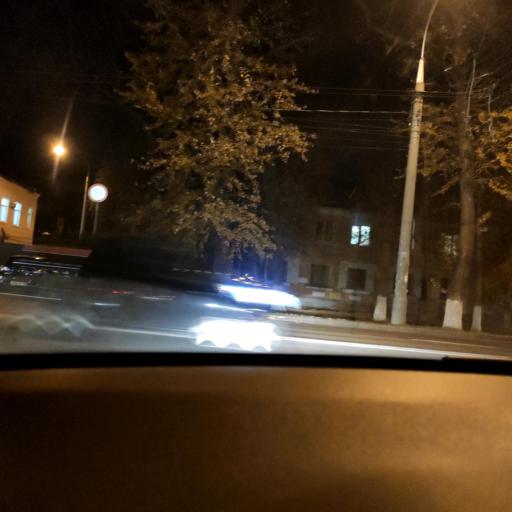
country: RU
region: Samara
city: Samara
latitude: 53.2210
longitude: 50.2608
